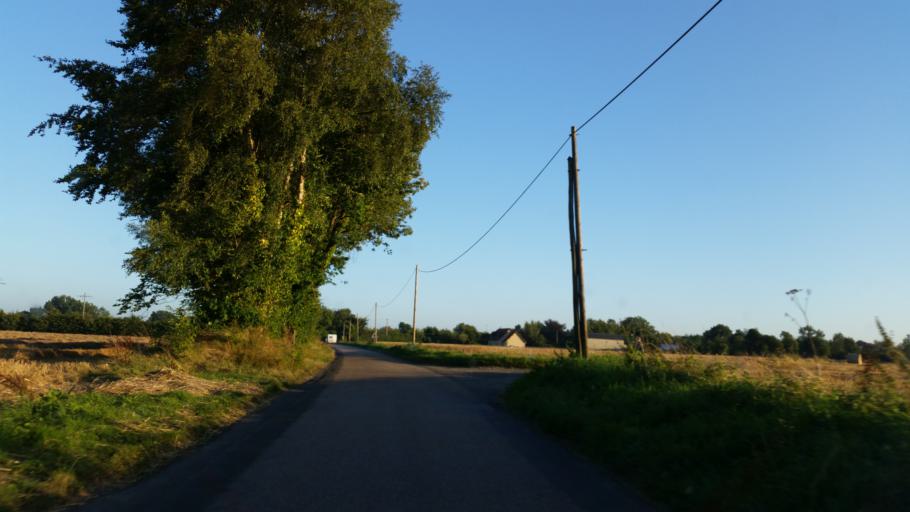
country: FR
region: Lower Normandy
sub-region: Departement du Calvados
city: Equemauville
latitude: 49.3855
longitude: 0.2264
